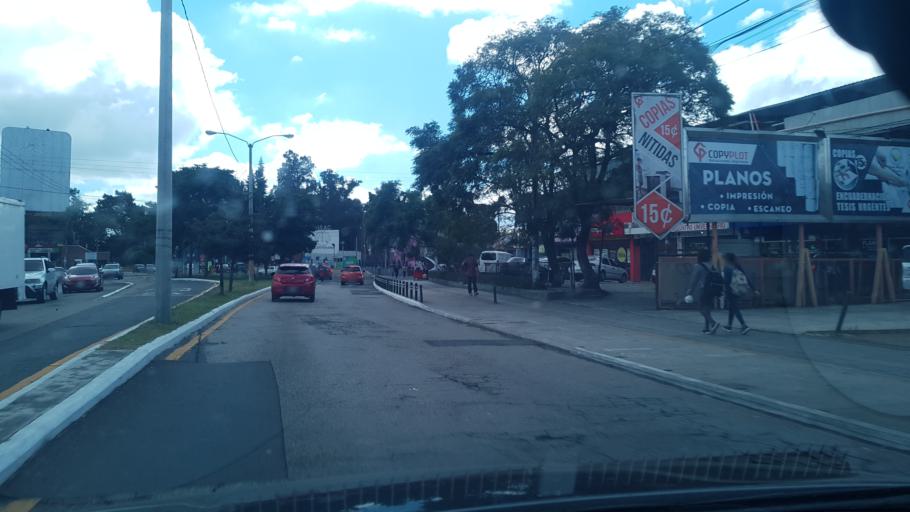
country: GT
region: Guatemala
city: Santa Catarina Pinula
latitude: 14.5909
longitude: -90.5513
